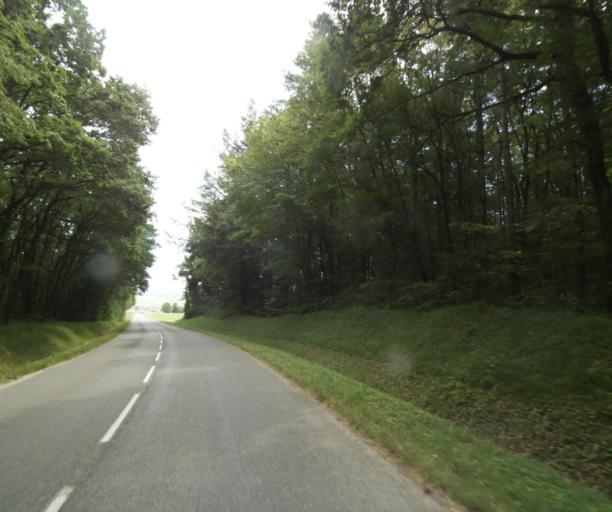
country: FR
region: Rhone-Alpes
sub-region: Departement de la Haute-Savoie
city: Douvaine
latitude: 46.3112
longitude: 6.2798
